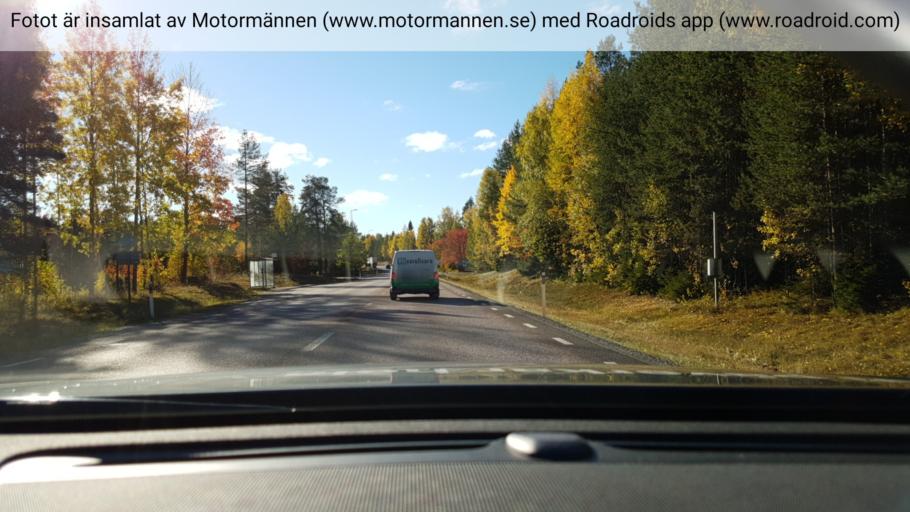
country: SE
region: Vaesterbotten
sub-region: Skelleftea Kommun
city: Burea
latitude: 64.6207
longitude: 21.1784
